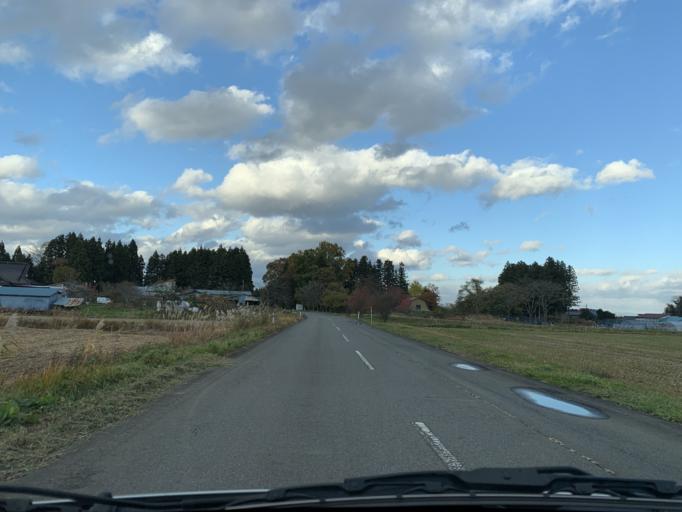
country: JP
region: Iwate
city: Mizusawa
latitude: 39.0983
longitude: 141.0142
